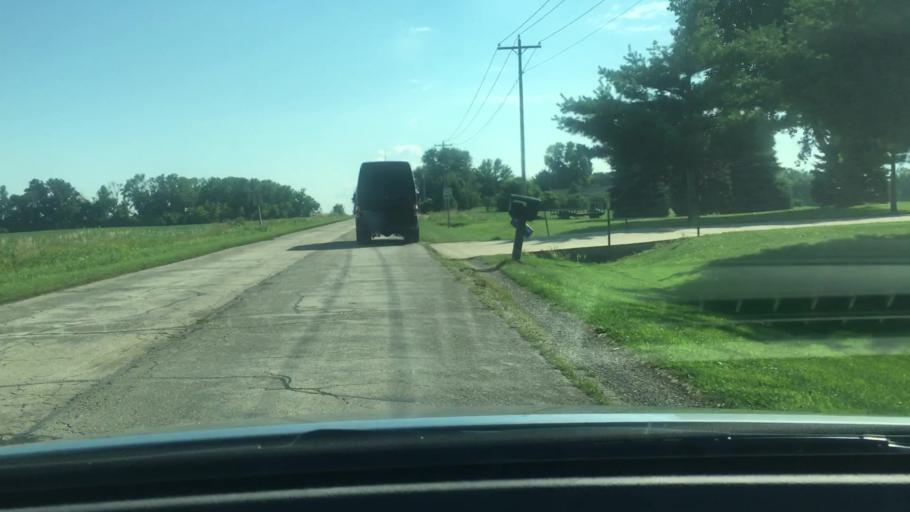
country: US
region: Wisconsin
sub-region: Winnebago County
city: Oshkosh
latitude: 43.9591
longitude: -88.5751
